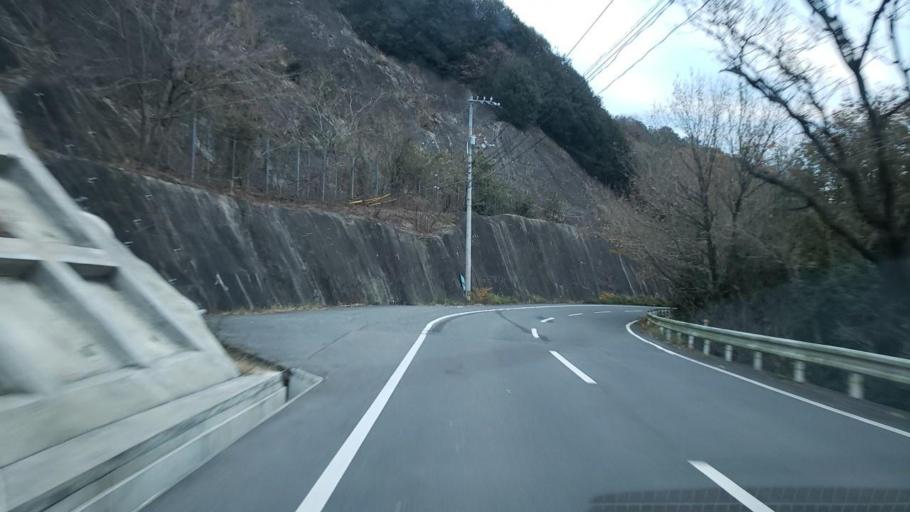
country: JP
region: Tokushima
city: Wakimachi
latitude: 34.1812
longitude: 134.2285
